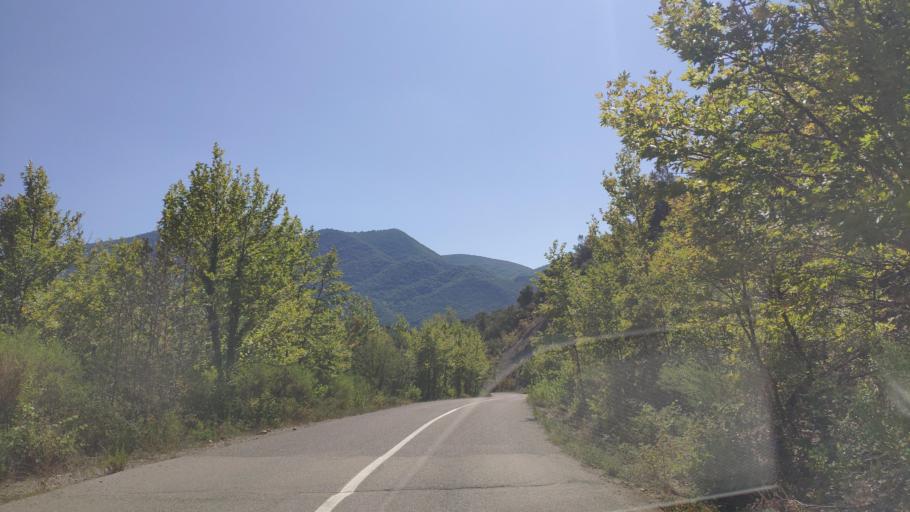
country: GR
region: Central Greece
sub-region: Nomos Evrytanias
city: Kerasochori
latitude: 38.9995
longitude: 21.5508
